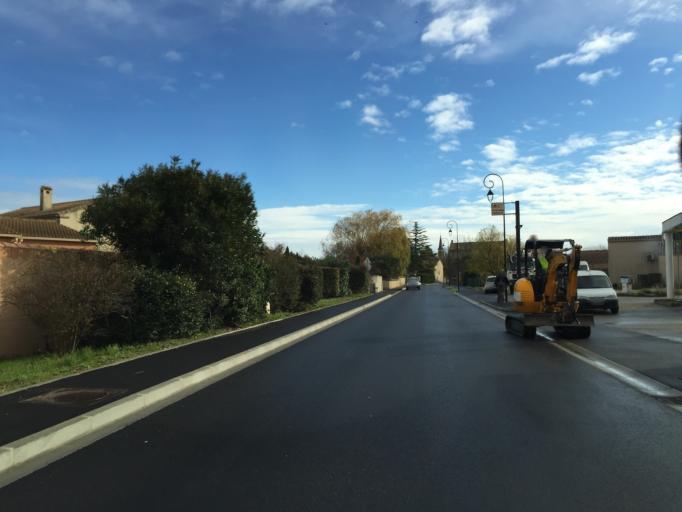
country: FR
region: Provence-Alpes-Cote d'Azur
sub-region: Departement du Vaucluse
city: Althen-des-Paluds
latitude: 43.9832
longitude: 4.9664
